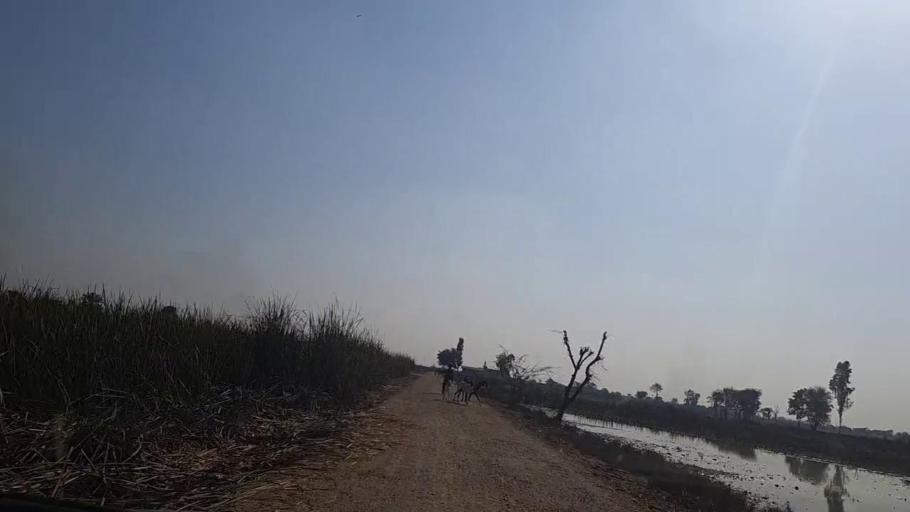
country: PK
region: Sindh
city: Sakrand
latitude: 26.0887
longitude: 68.3704
